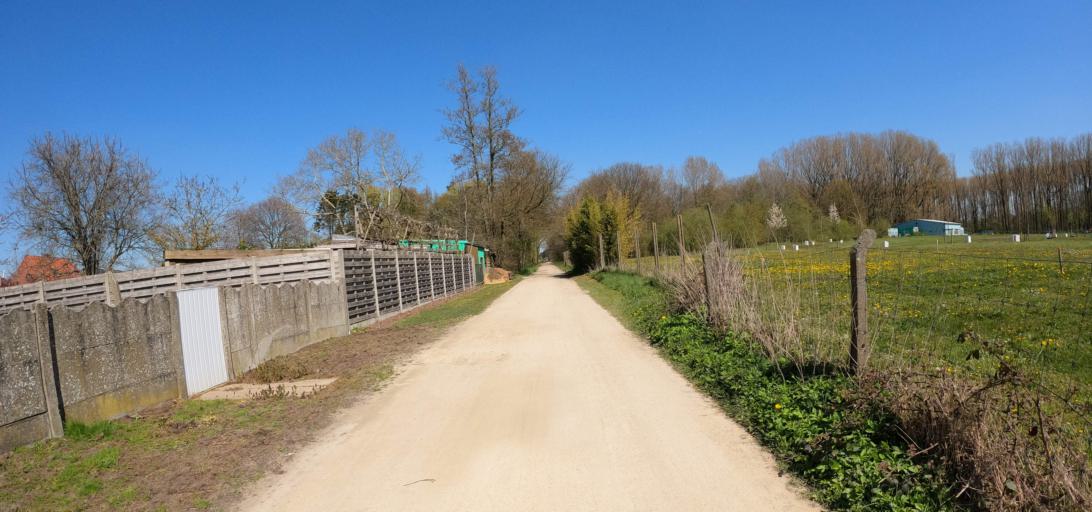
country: BE
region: Flanders
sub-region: Provincie Antwerpen
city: Rijkevorsel
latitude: 51.3322
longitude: 4.7924
